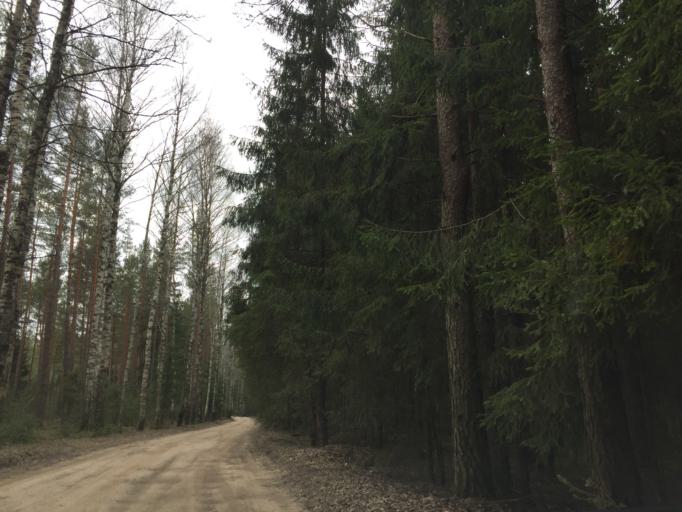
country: LV
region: Incukalns
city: Vangazi
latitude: 57.1012
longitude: 24.5457
